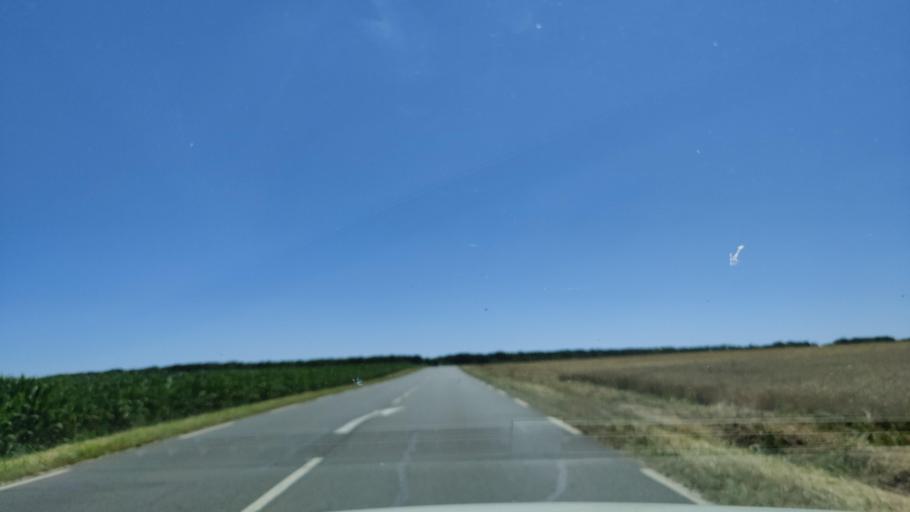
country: FR
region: Ile-de-France
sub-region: Departement de l'Essonne
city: Fontenay-les-Briis
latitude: 48.6382
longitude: 2.1829
